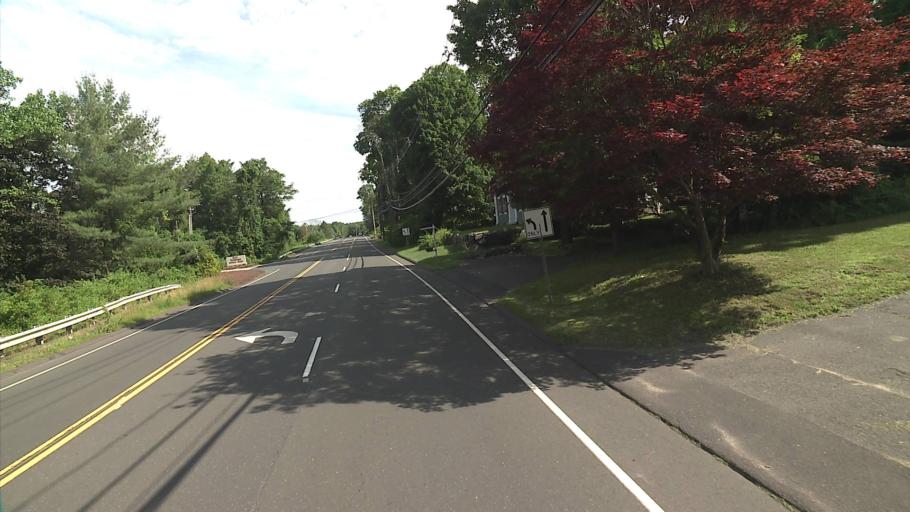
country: US
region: Connecticut
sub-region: New Haven County
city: Waterbury
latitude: 41.5520
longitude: -73.0917
